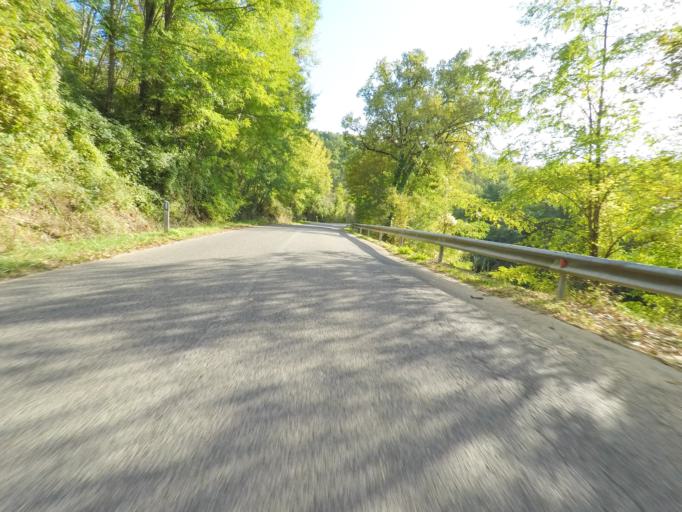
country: IT
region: Tuscany
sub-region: Provincia di Siena
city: Radda in Chianti
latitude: 43.4969
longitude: 11.3923
